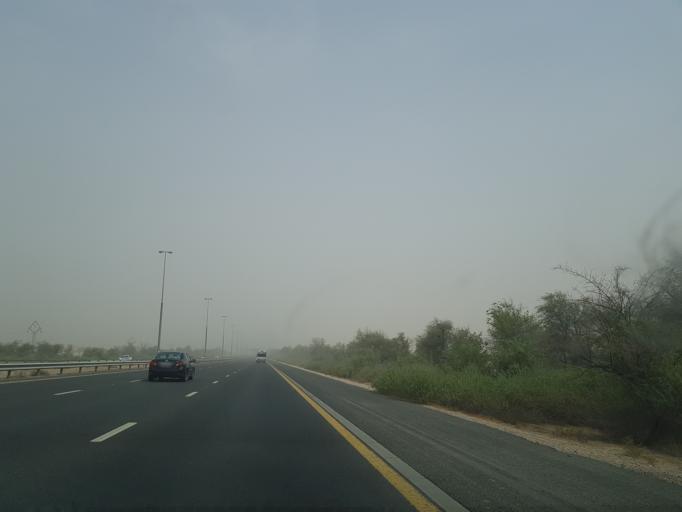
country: AE
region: Dubai
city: Dubai
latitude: 24.9337
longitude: 55.5156
